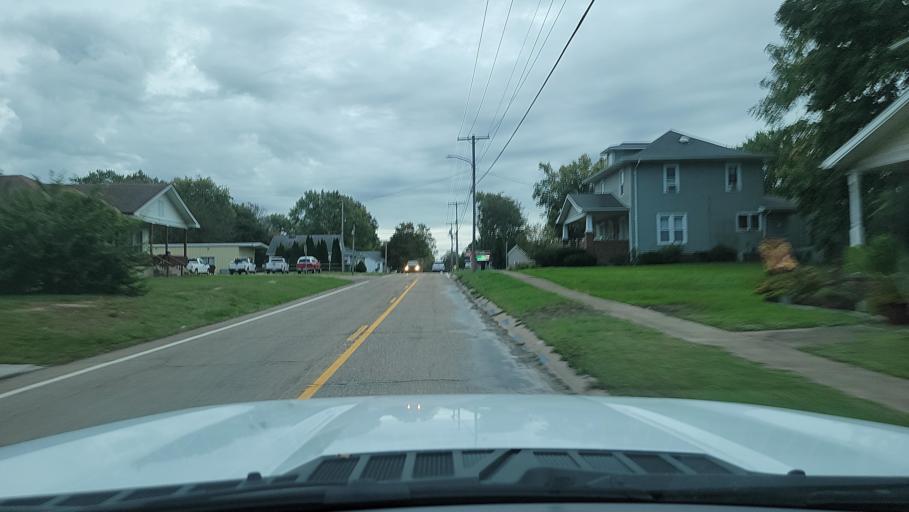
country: US
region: Illinois
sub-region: Schuyler County
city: Rushville
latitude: 40.1177
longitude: -90.5695
